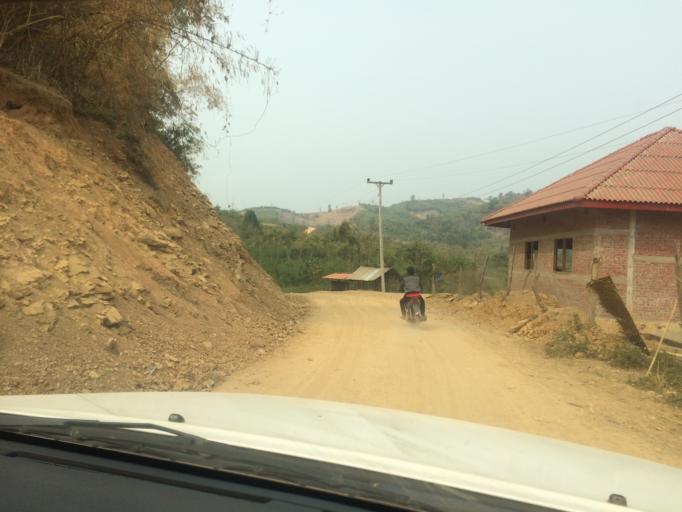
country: LA
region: Loungnamtha
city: Muang Nale
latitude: 20.4337
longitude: 101.7095
